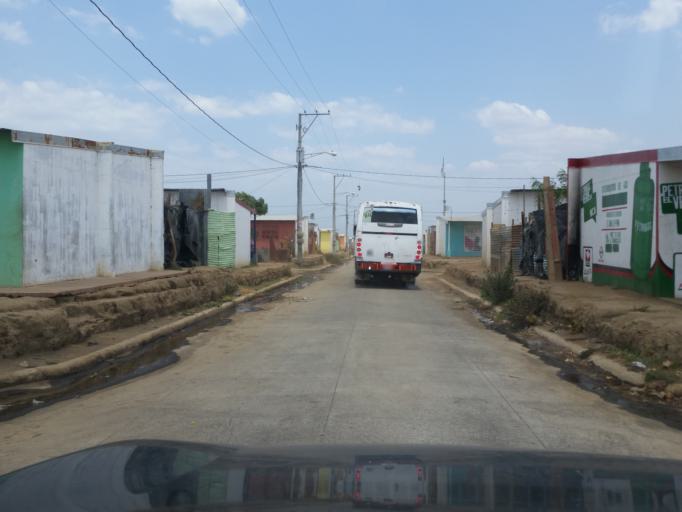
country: NI
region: Managua
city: Managua
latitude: 12.1270
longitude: -86.1583
